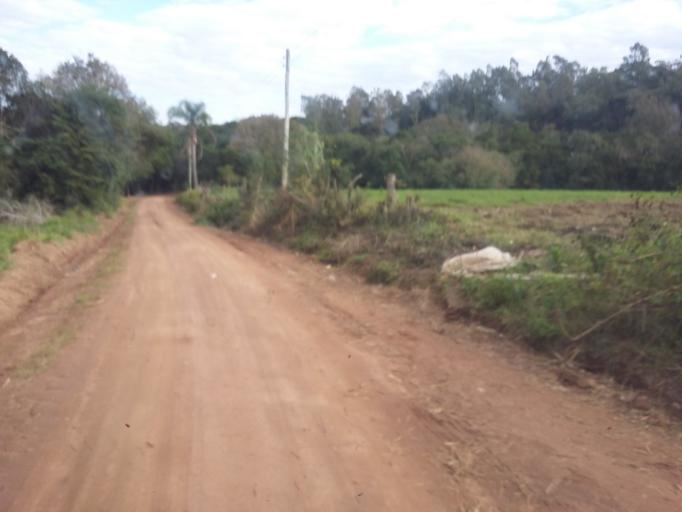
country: BR
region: Rio Grande do Sul
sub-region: Camaqua
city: Camaqua
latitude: -30.7108
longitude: -51.7747
